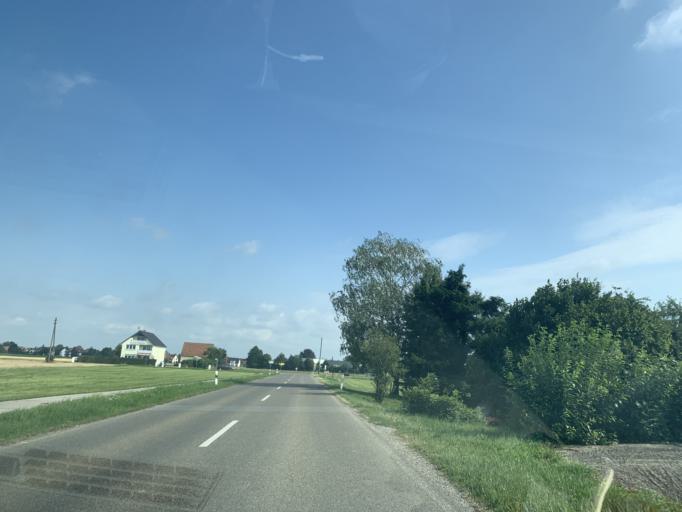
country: DE
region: Bavaria
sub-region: Swabia
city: Kissing
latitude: 48.2940
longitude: 10.9822
